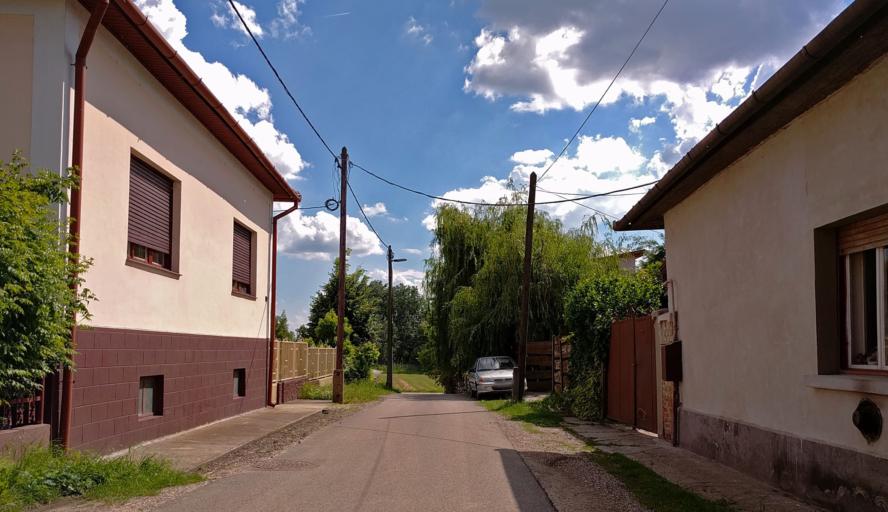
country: HU
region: Bacs-Kiskun
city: Tiszakecske
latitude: 46.9297
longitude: 20.0963
